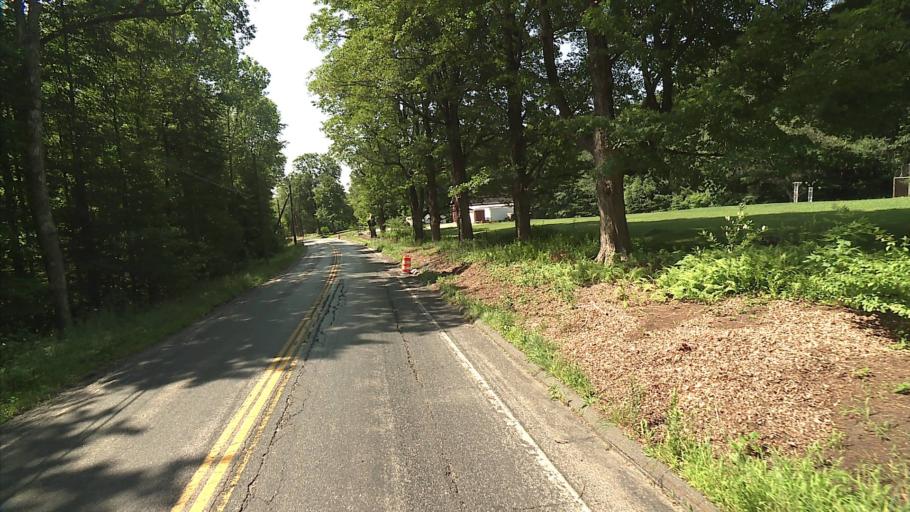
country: US
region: Connecticut
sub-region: Litchfield County
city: Winchester Center
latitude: 41.9398
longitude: -73.2085
